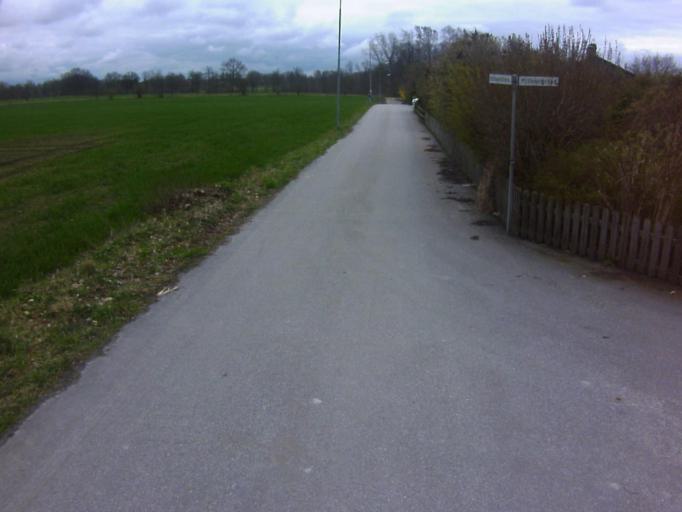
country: SE
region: Skane
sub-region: Lunds Kommun
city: Lund
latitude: 55.7886
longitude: 13.2072
